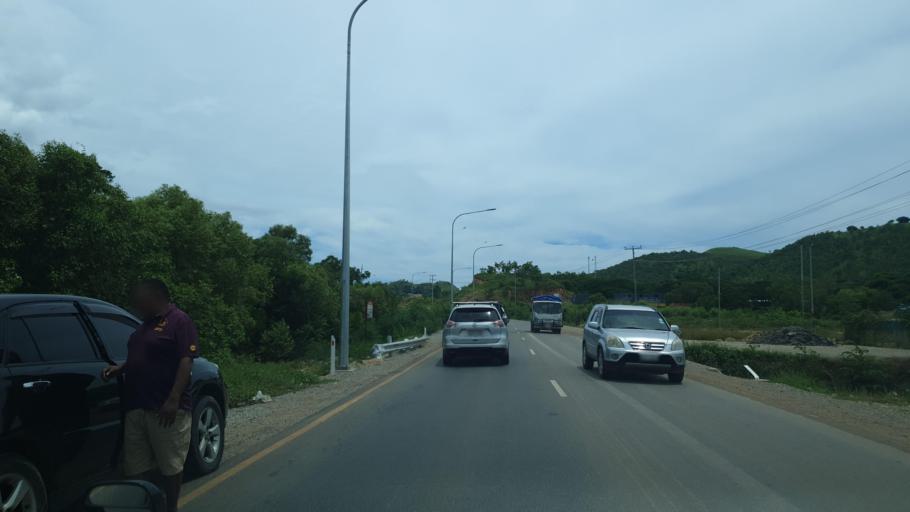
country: PG
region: National Capital
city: Port Moresby
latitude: -9.5022
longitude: 147.2349
